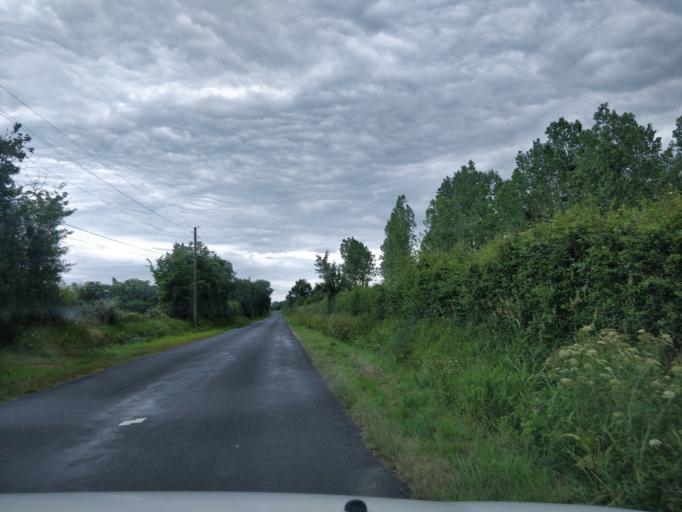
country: FR
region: Pays de la Loire
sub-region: Departement de Maine-et-Loire
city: Grez-Neuville
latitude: 47.6269
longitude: -0.6259
